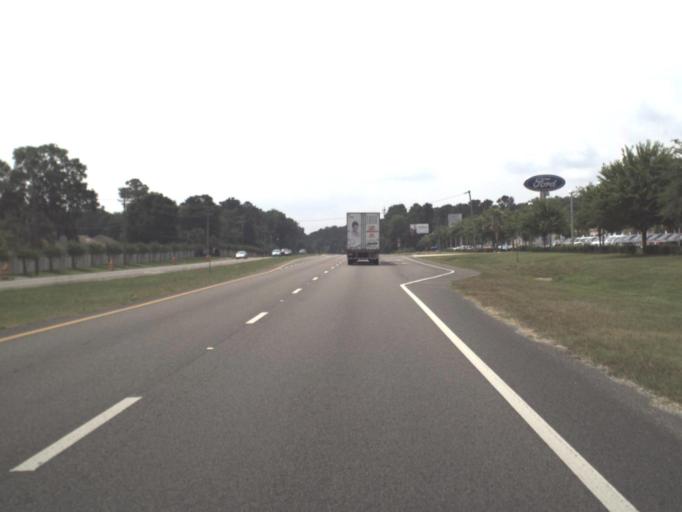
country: US
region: Florida
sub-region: Clay County
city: Green Cove Springs
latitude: 30.0172
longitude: -81.7029
